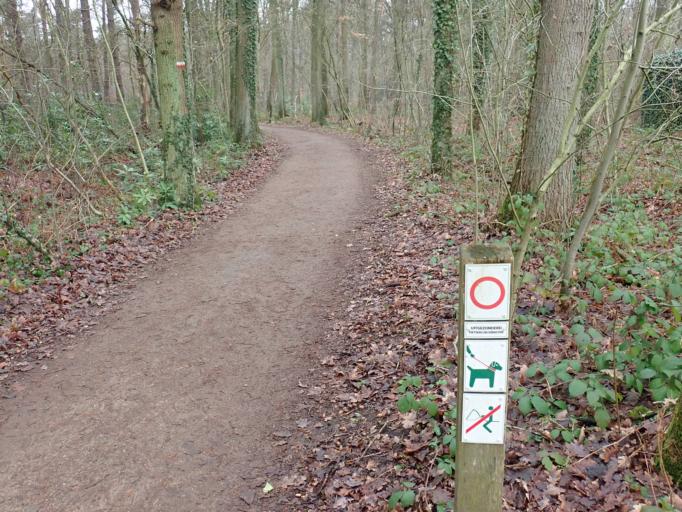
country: BE
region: Flanders
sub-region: Provincie Antwerpen
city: Schilde
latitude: 51.2201
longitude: 4.6133
